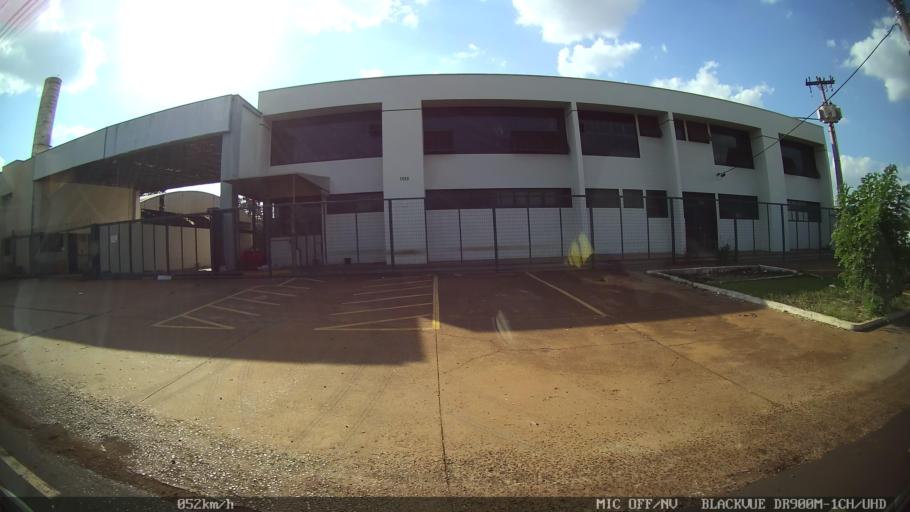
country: BR
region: Sao Paulo
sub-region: Ribeirao Preto
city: Ribeirao Preto
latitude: -21.1779
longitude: -47.8304
